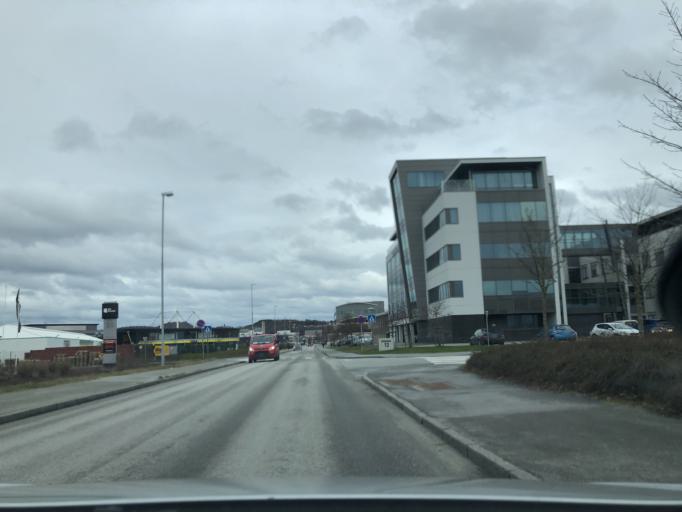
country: NO
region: Rogaland
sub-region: Sandnes
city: Sandnes
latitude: 58.8817
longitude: 5.7212
